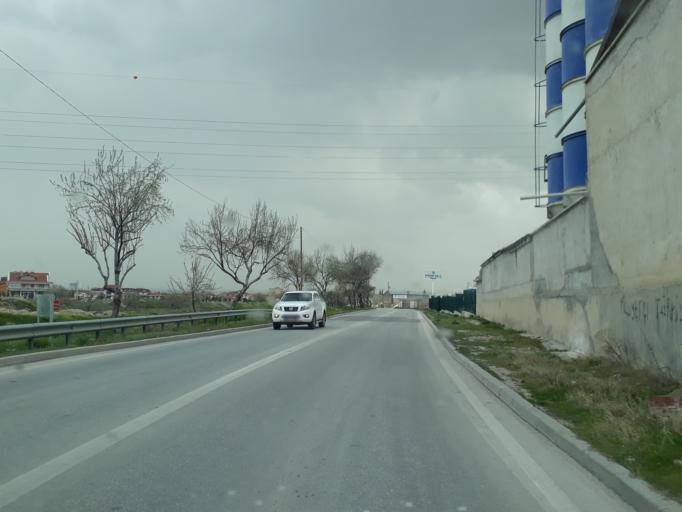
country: TR
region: Konya
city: Selcuklu
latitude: 37.9200
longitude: 32.4683
